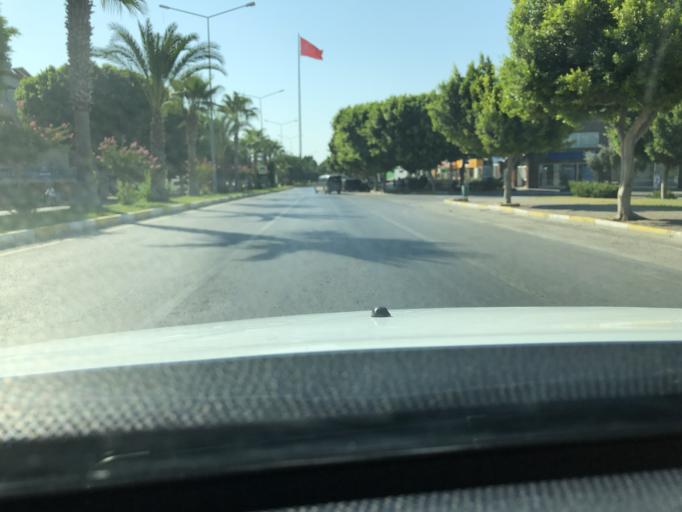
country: TR
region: Antalya
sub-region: Manavgat
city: Side
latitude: 36.7783
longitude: 31.3958
